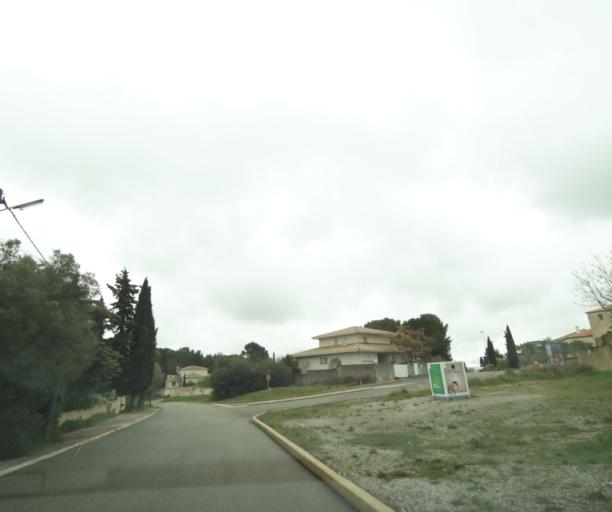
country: FR
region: Languedoc-Roussillon
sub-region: Departement de l'Herault
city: Cournonsec
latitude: 43.5602
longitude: 3.7082
